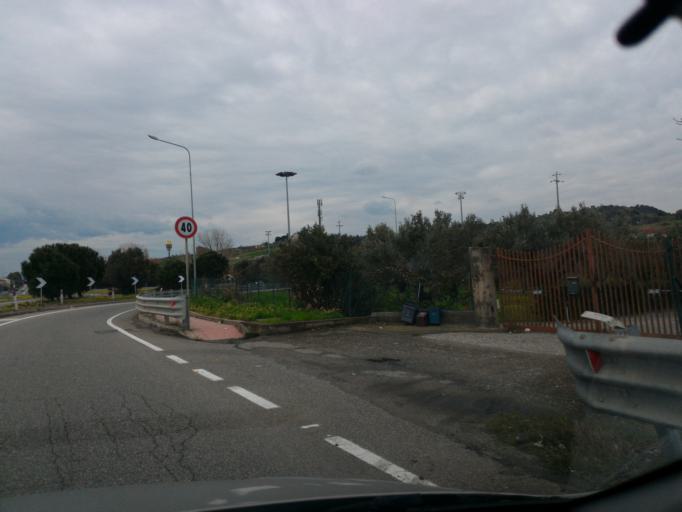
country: IT
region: Calabria
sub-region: Provincia di Catanzaro
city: Barone
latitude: 38.8433
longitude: 16.6507
